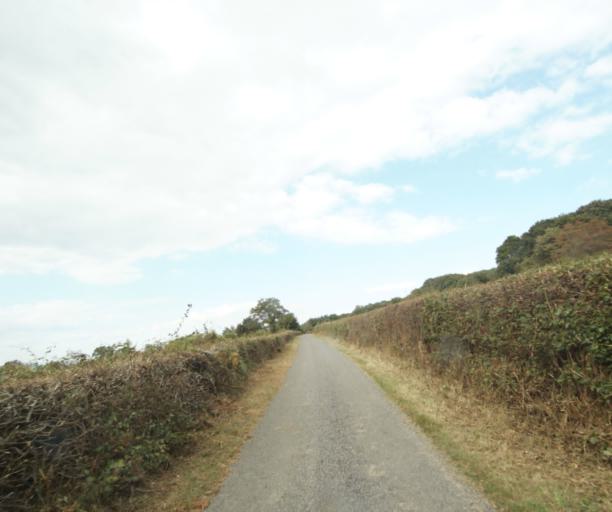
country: FR
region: Bourgogne
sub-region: Departement de Saone-et-Loire
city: Palinges
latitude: 46.5210
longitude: 4.2906
